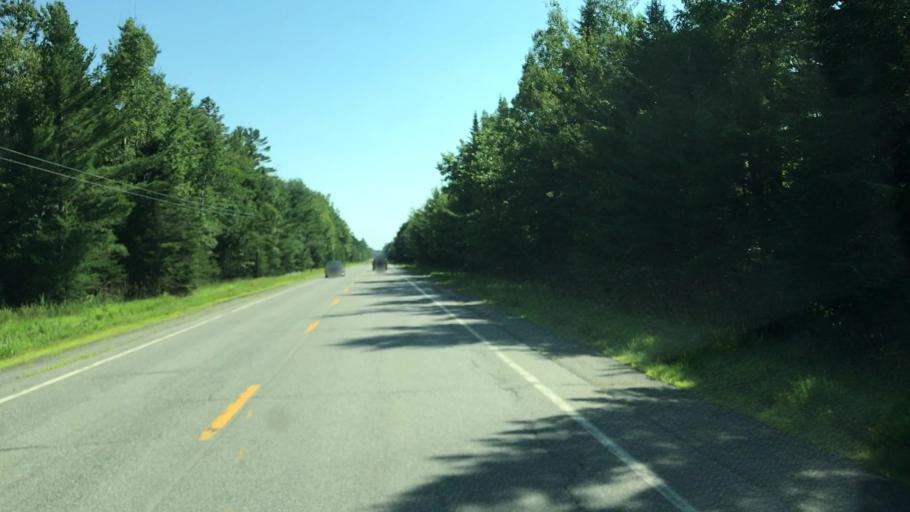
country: US
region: Maine
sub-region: Penobscot County
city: Enfield
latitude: 45.3139
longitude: -68.6050
